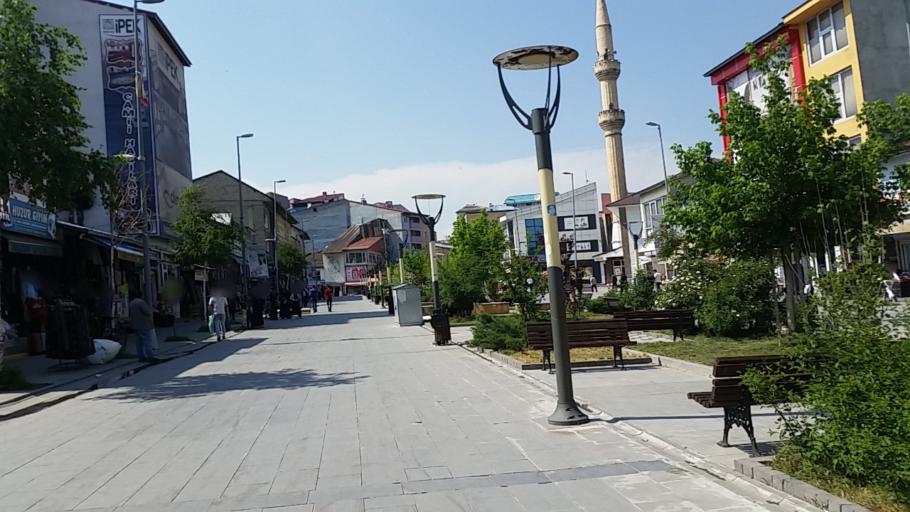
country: TR
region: Agri
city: Agri
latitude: 39.7167
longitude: 43.0519
